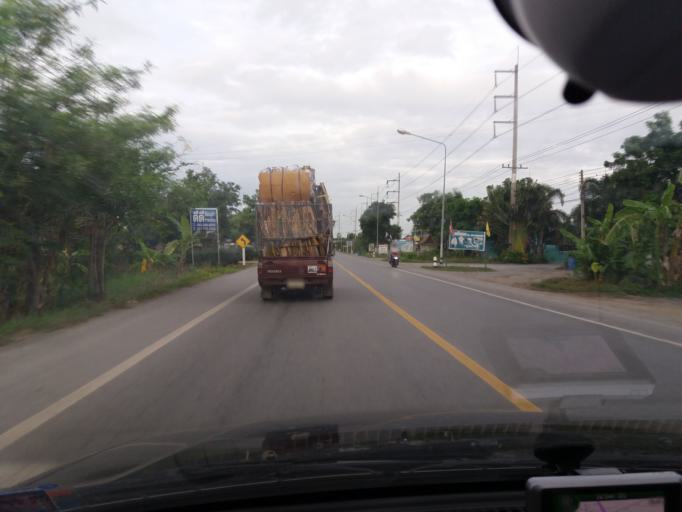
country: TH
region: Suphan Buri
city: U Thong
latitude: 14.4710
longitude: 99.9348
